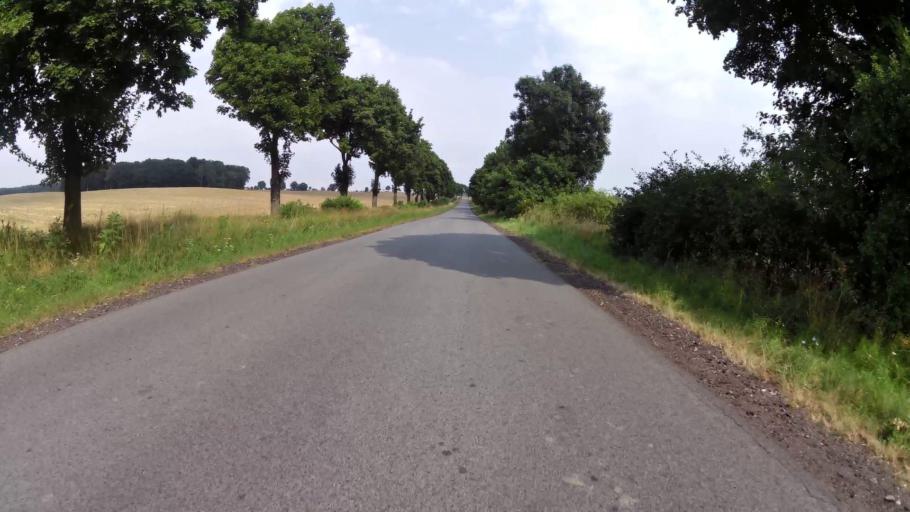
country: PL
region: West Pomeranian Voivodeship
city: Trzcinsko Zdroj
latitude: 52.9219
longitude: 14.6480
